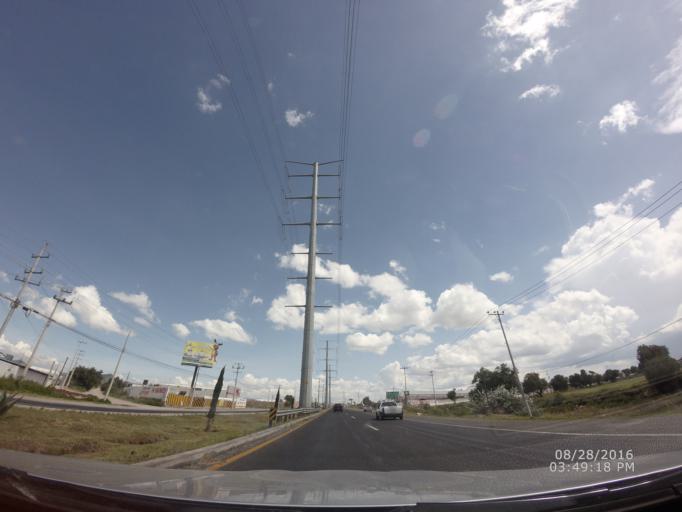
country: MX
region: Hidalgo
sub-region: Mineral de la Reforma
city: Los Tuzos
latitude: 20.0455
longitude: -98.7361
